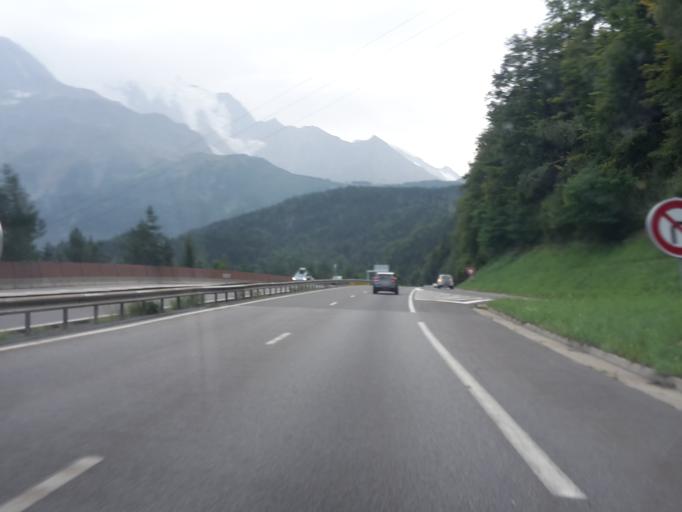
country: FR
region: Rhone-Alpes
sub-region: Departement de la Haute-Savoie
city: Les Houches
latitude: 45.9237
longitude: 6.7626
